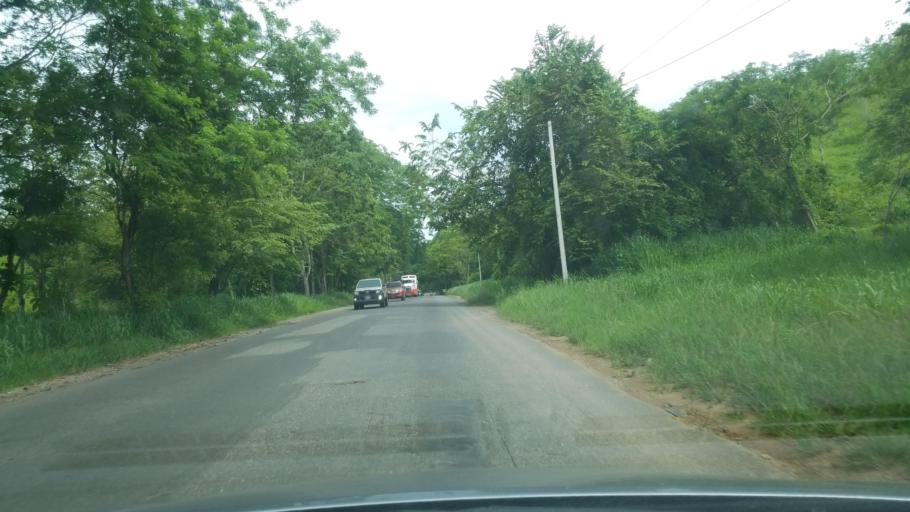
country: HN
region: Santa Barbara
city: Camalote
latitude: 15.3322
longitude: -88.3442
